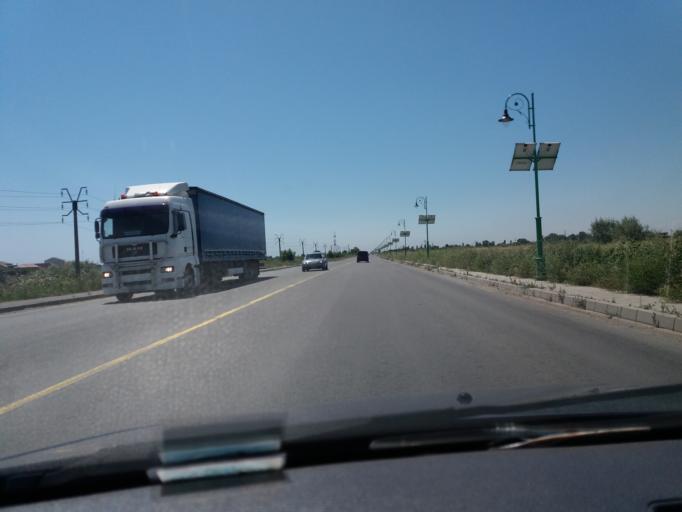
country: RO
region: Constanta
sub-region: Comuna Navodari
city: Navodari
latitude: 44.3070
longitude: 28.6154
